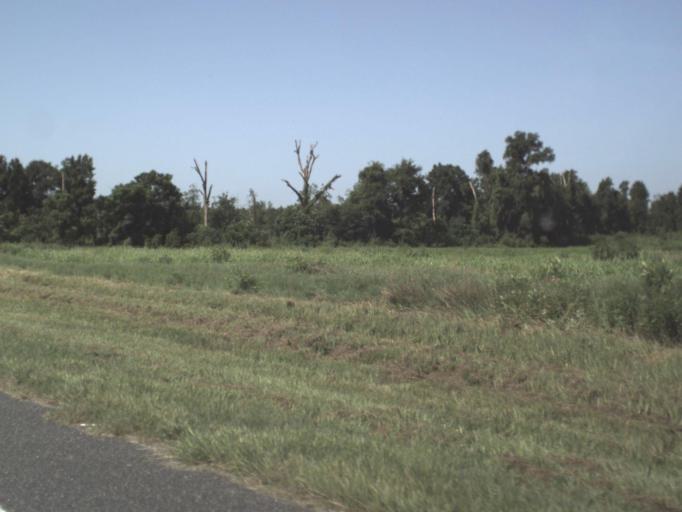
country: US
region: Florida
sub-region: Alachua County
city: High Springs
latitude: 29.9410
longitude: -82.7136
